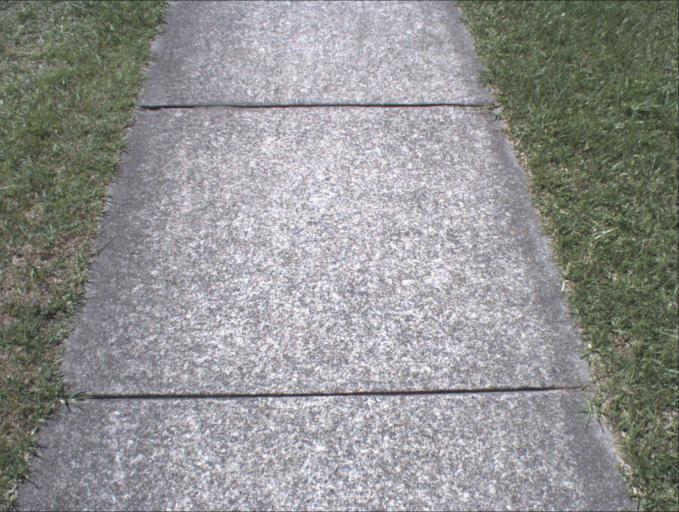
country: AU
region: Queensland
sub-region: Logan
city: Beenleigh
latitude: -27.7015
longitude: 153.1684
